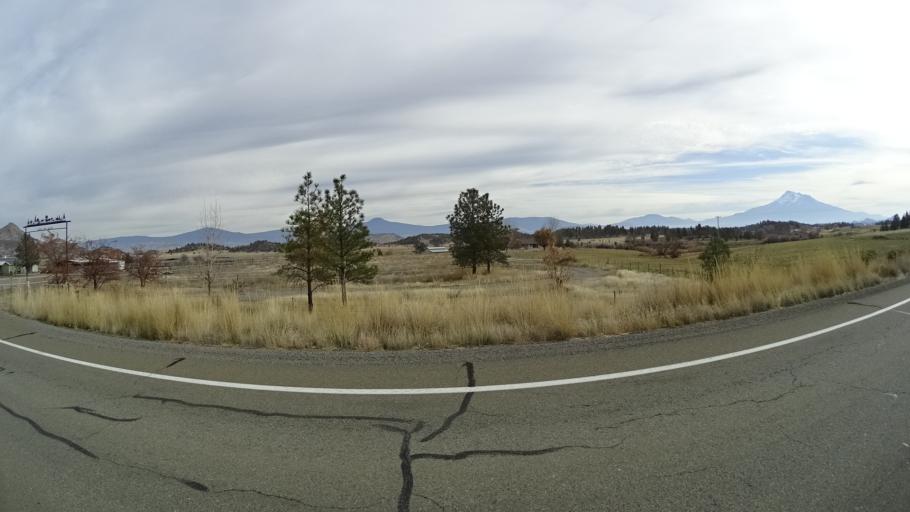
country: US
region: California
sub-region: Siskiyou County
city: Montague
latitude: 41.6904
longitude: -122.5350
